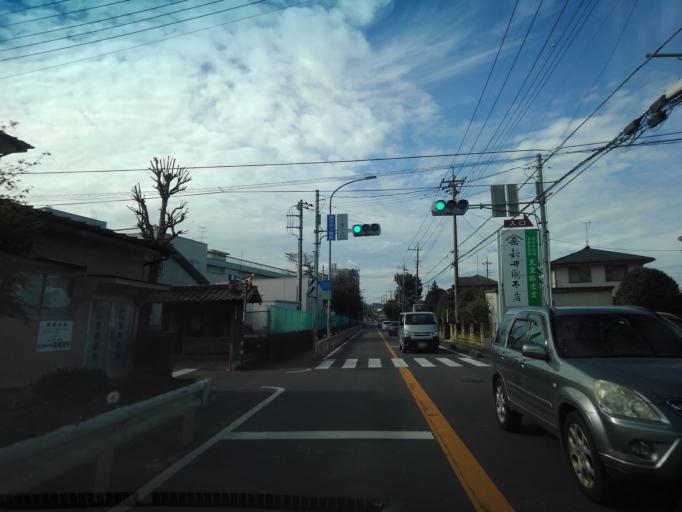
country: JP
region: Saitama
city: Sayama
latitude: 35.7944
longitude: 139.4050
